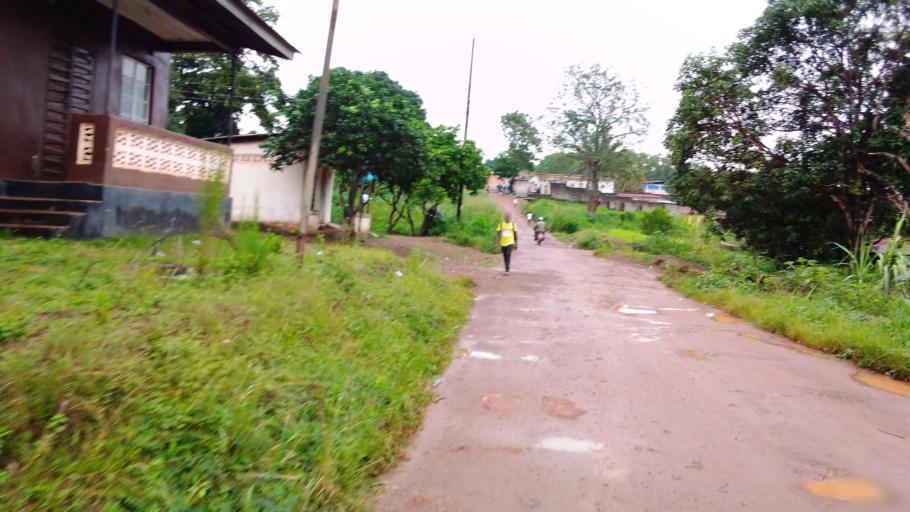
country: SL
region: Eastern Province
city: Kenema
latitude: 7.8961
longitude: -11.1808
